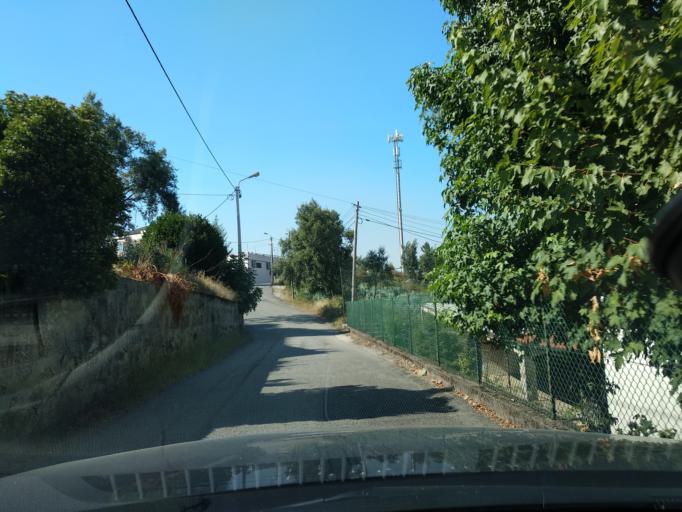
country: PT
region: Porto
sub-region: Paredes
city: Rebordosa
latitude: 41.2237
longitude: -8.4147
